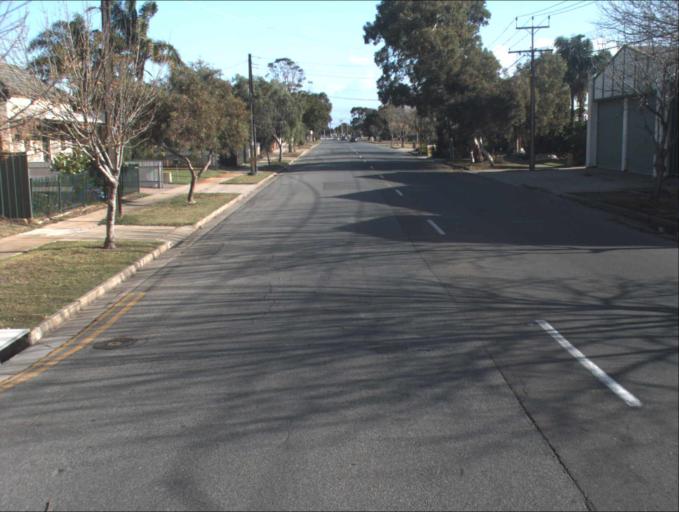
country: AU
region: South Australia
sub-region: Port Adelaide Enfield
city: Cheltenham
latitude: -34.8562
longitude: 138.5063
